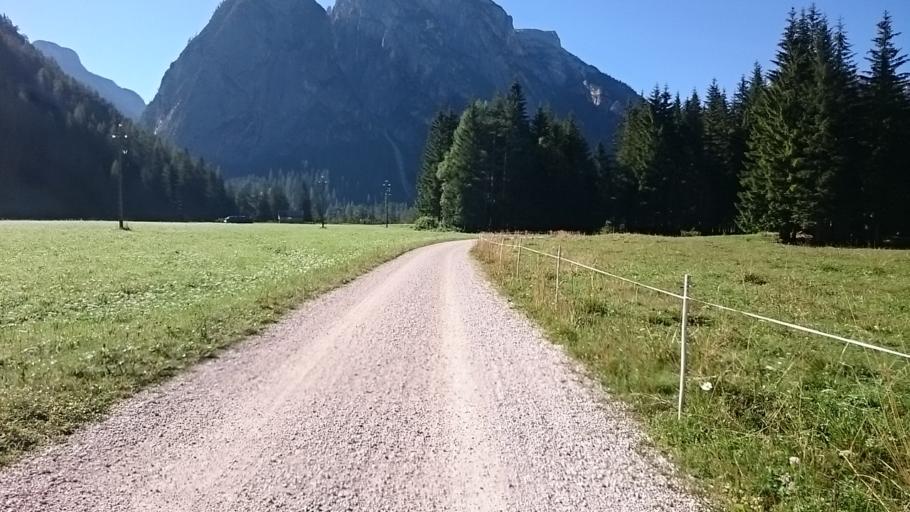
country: IT
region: Trentino-Alto Adige
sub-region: Bolzano
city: Dobbiaco
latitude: 46.6431
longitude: 12.2329
